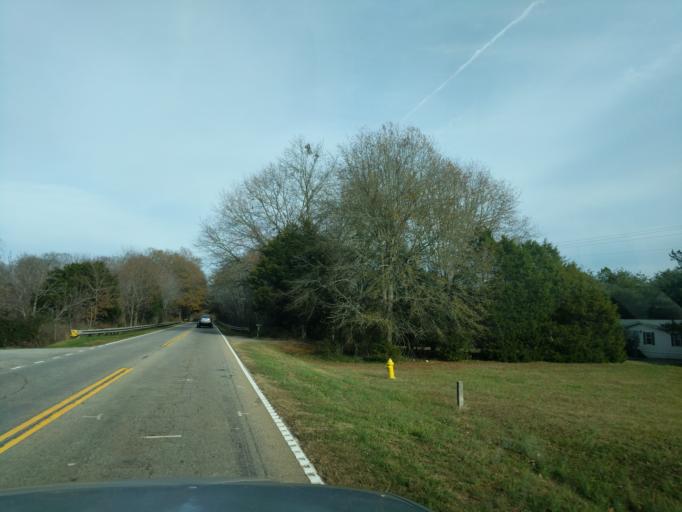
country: US
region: South Carolina
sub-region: Pickens County
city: Liberty
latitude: 34.7076
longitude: -82.6187
